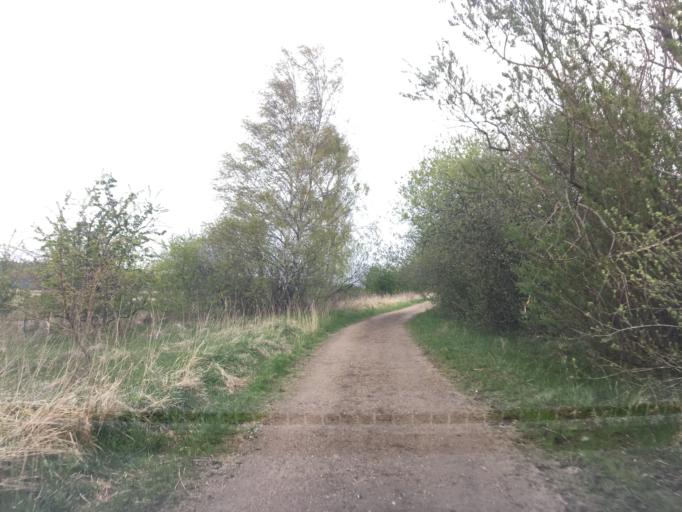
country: DK
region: Capital Region
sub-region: Tarnby Kommune
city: Tarnby
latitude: 55.5860
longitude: 12.5682
